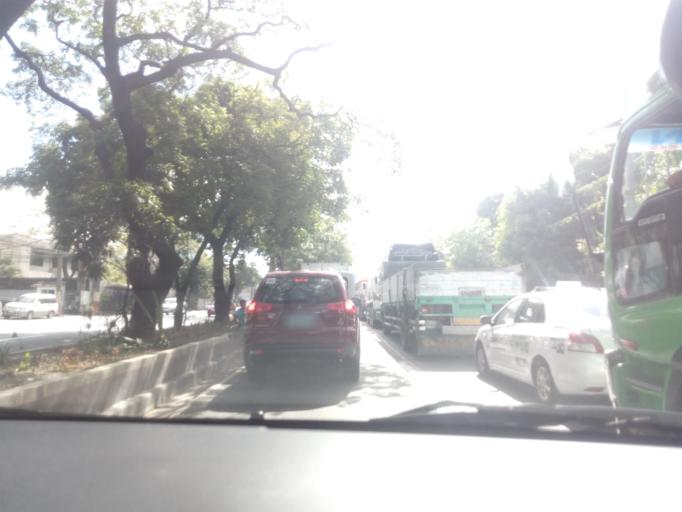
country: PH
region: Metro Manila
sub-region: Pasig
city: Pasig City
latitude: 14.5825
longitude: 121.0767
